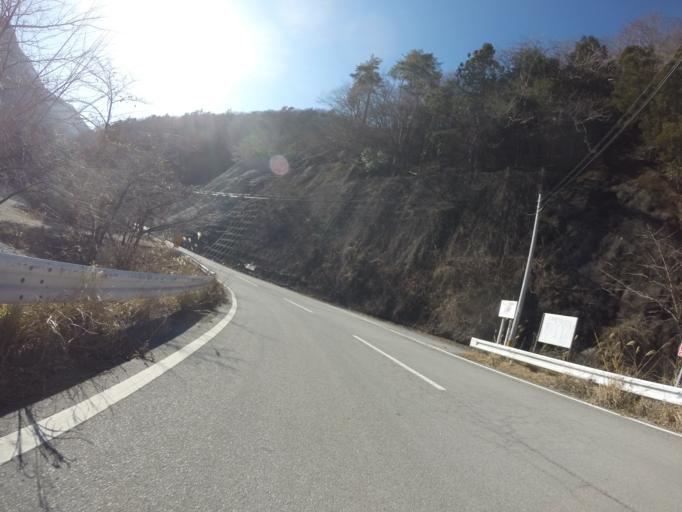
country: JP
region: Yamanashi
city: Ryuo
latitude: 35.4100
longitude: 138.3278
